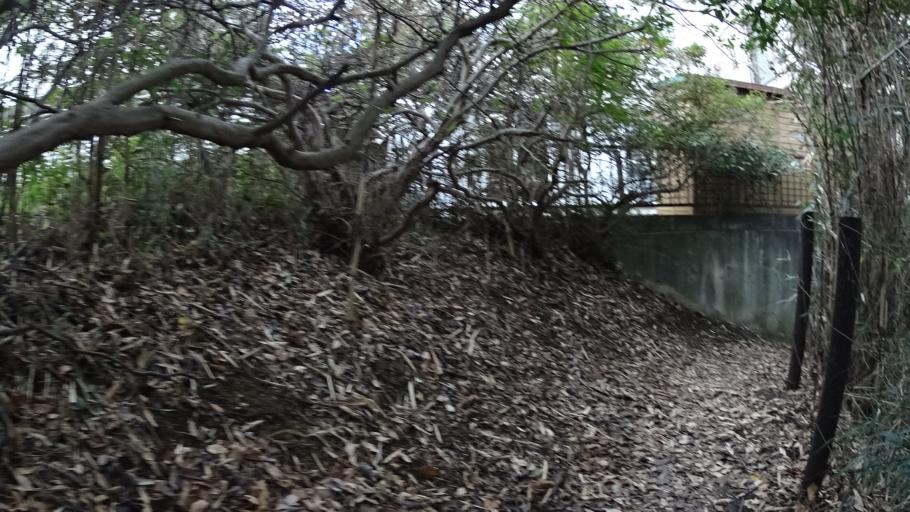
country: JP
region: Kanagawa
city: Yokohama
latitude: 35.4149
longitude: 139.5552
